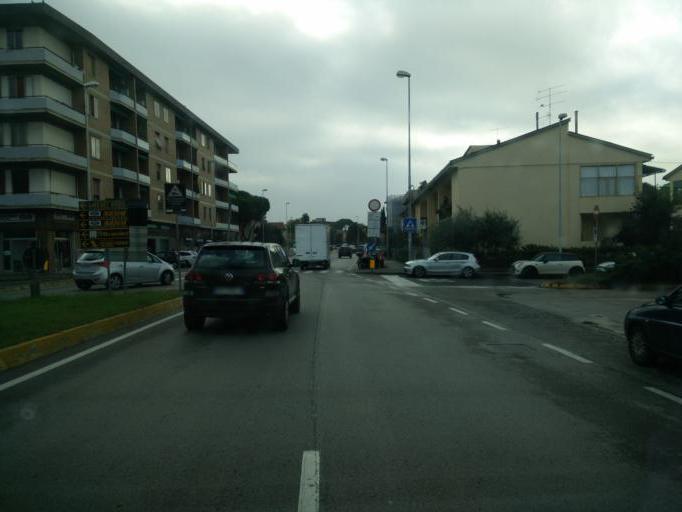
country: IT
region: Tuscany
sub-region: Province of Florence
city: Mantignano-Ugnano
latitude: 43.8000
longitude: 11.1926
